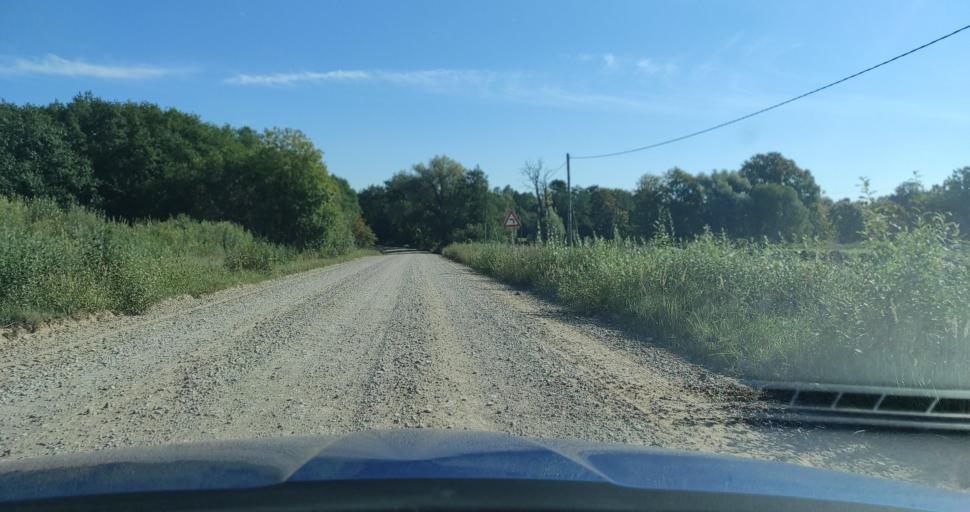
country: LV
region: Aizpute
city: Aizpute
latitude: 56.8103
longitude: 21.4761
